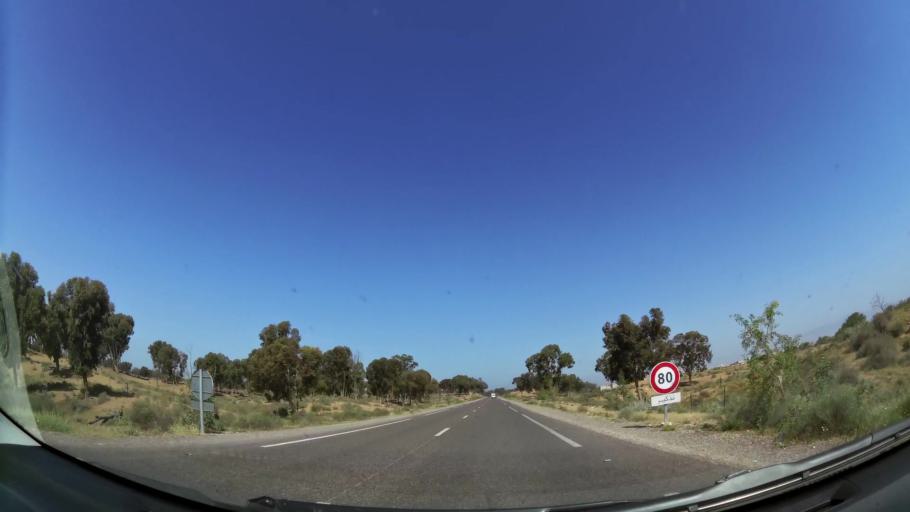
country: MA
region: Souss-Massa-Draa
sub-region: Inezgane-Ait Mellou
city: Inezgane
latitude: 30.3143
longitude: -9.5212
